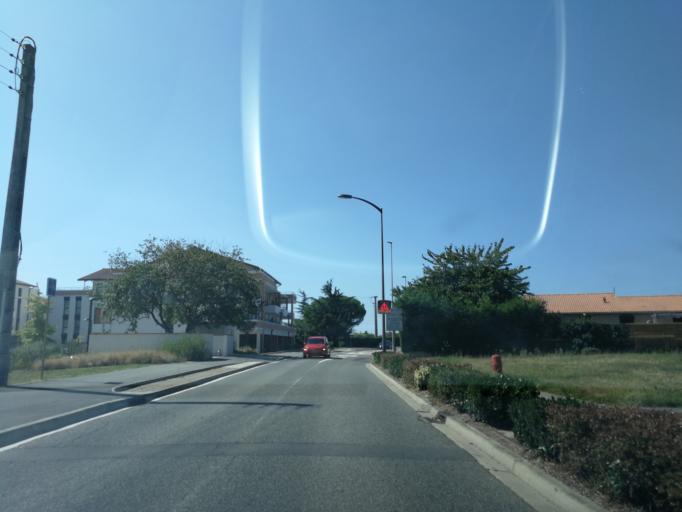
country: FR
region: Midi-Pyrenees
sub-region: Departement de la Haute-Garonne
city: Saint-Orens-de-Gameville
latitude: 43.5806
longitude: 1.5369
